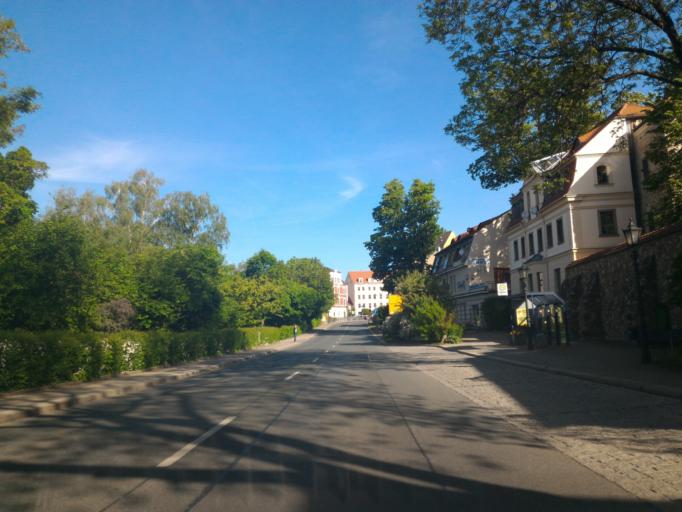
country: DE
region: Saxony
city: Lobau
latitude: 51.0942
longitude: 14.6657
